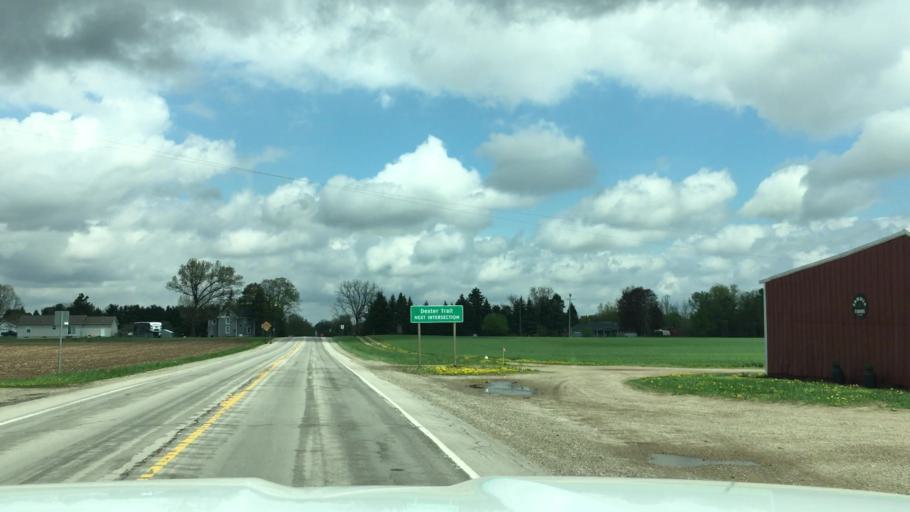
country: US
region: Michigan
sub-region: Ingham County
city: Stockbridge
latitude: 42.4663
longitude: -84.1901
